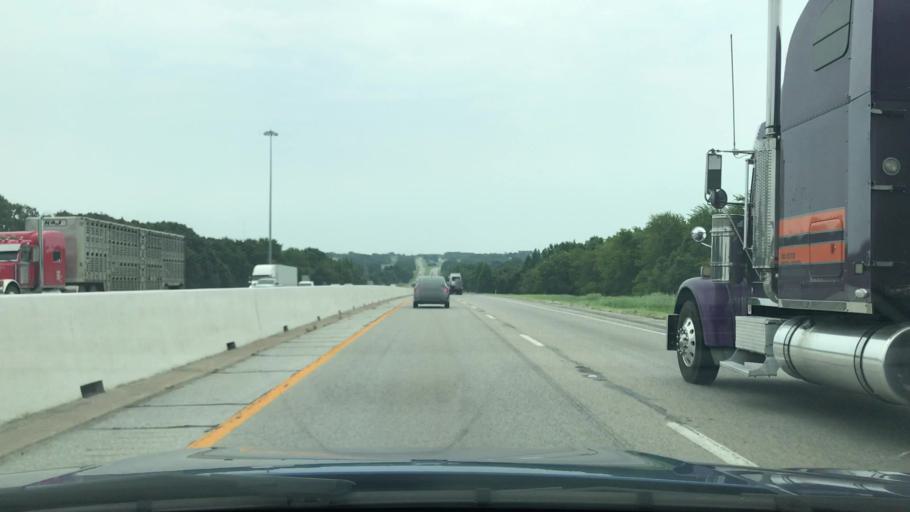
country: US
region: Texas
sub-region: Smith County
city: Hideaway
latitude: 32.4833
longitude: -95.5209
